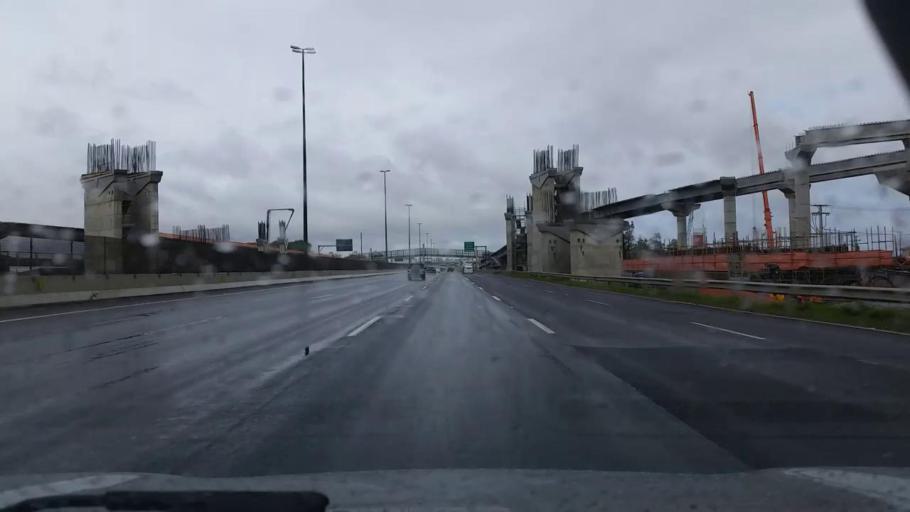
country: BR
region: Rio Grande do Sul
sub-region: Porto Alegre
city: Porto Alegre
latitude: -29.9871
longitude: -51.2033
